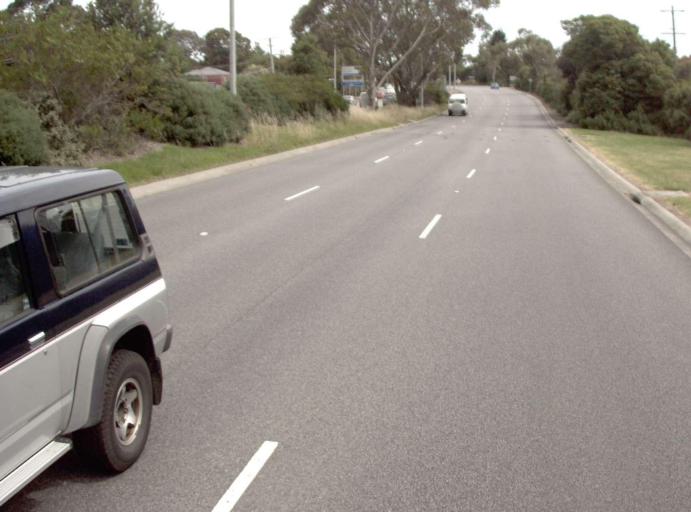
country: AU
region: Victoria
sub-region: Frankston
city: Frankston South
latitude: -38.1750
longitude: 145.1390
